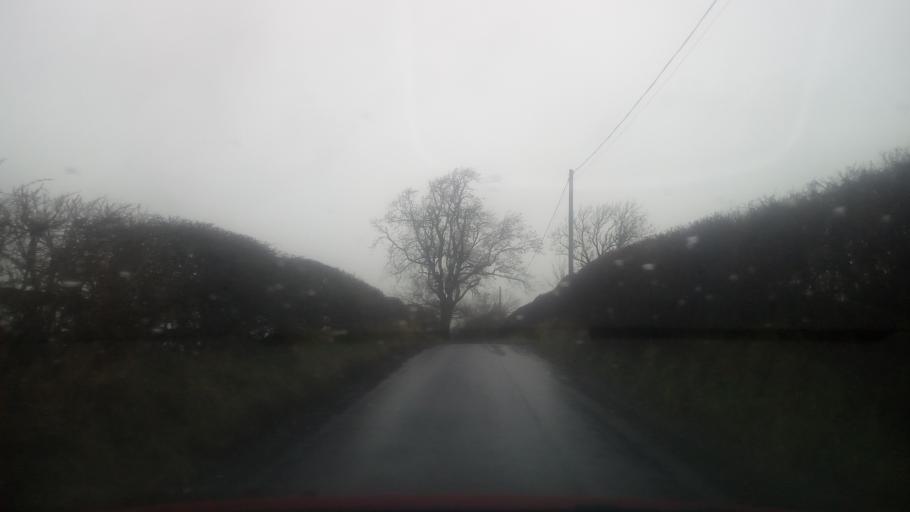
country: GB
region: Scotland
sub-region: The Scottish Borders
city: Earlston
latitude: 55.6153
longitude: -2.6624
